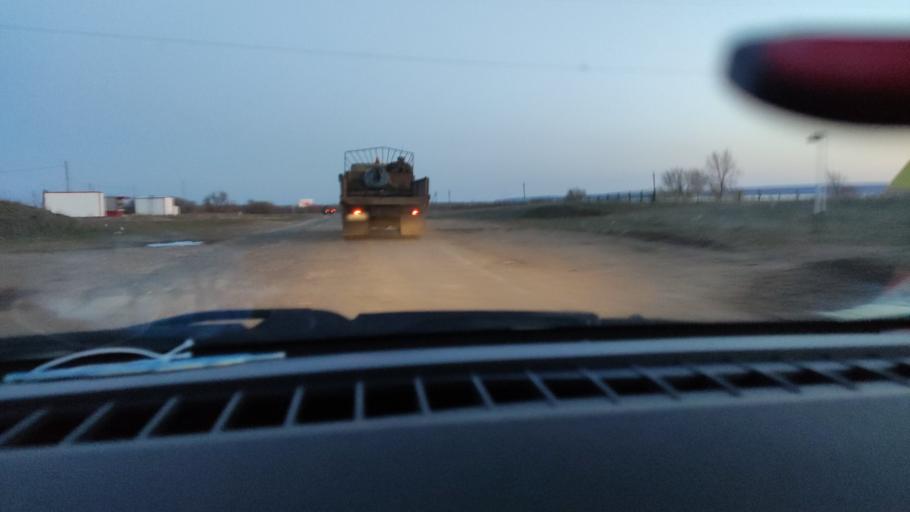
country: RU
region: Saratov
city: Rovnoye
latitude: 51.0177
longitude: 46.0944
